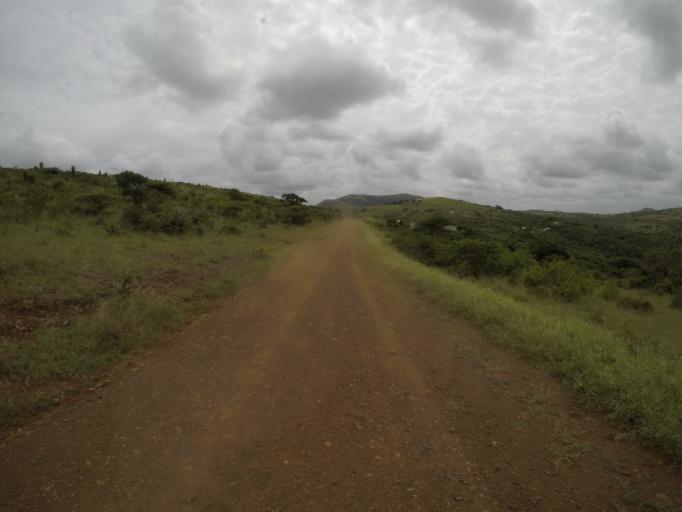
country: ZA
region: KwaZulu-Natal
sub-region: uThungulu District Municipality
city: Empangeni
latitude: -28.6247
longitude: 31.8895
